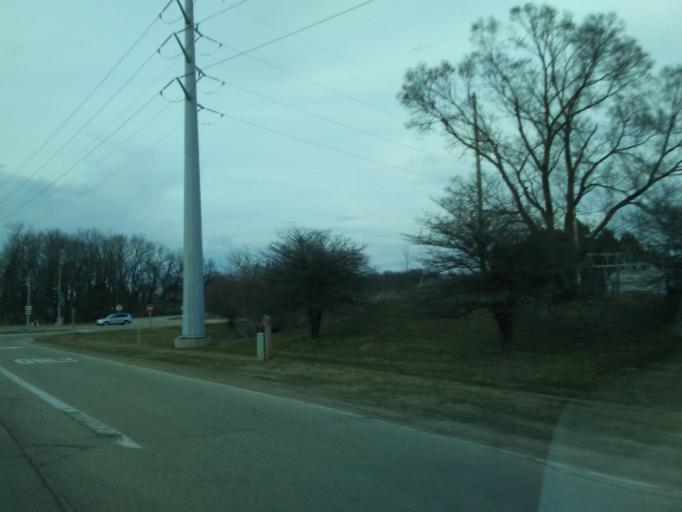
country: US
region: Wisconsin
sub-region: Dane County
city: Verona
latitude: 43.0153
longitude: -89.5335
